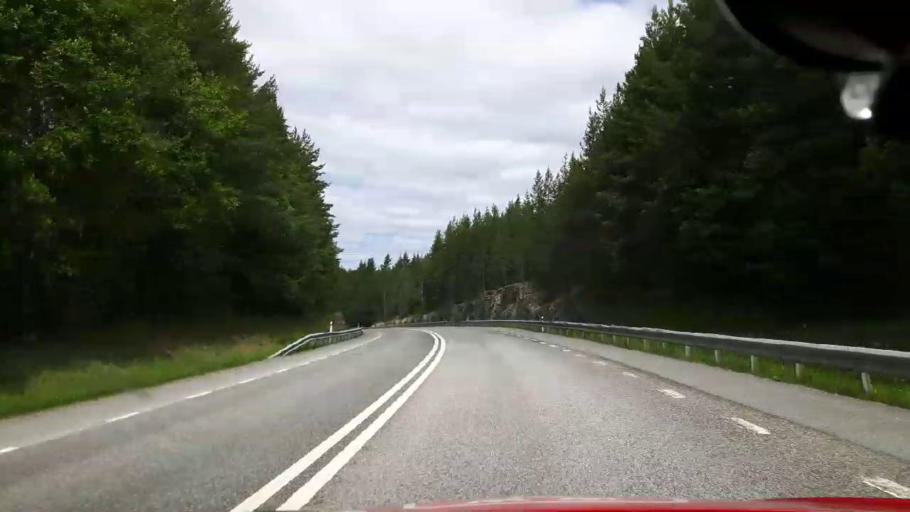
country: SE
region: Jaemtland
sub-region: Braecke Kommun
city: Braecke
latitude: 62.7367
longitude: 15.4328
